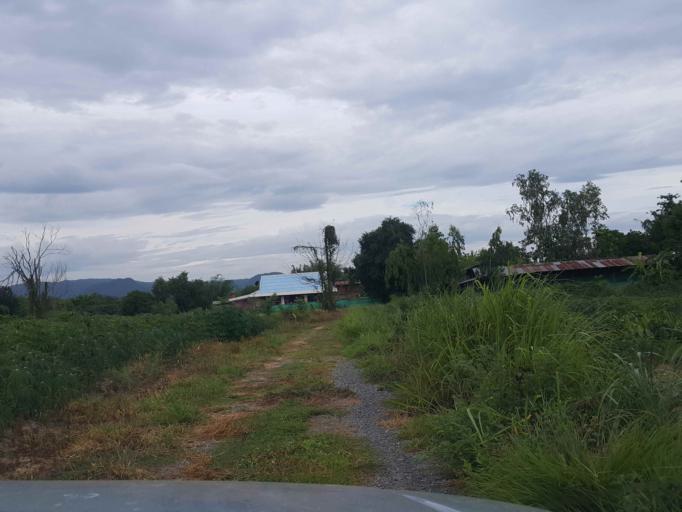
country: TH
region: Sukhothai
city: Thung Saliam
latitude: 17.3235
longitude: 99.4454
